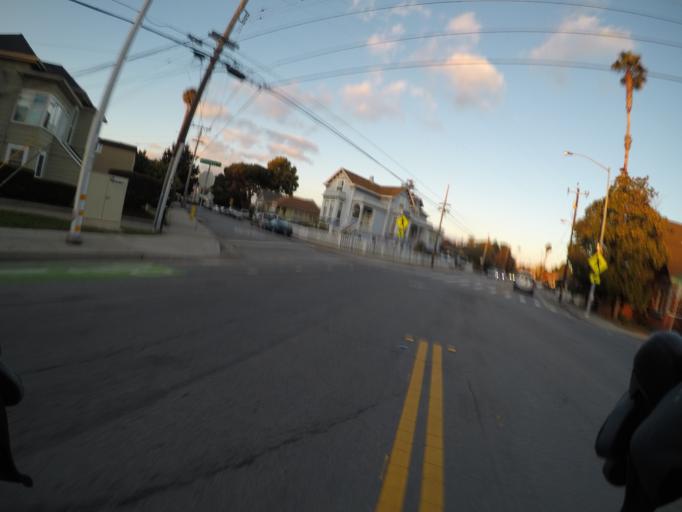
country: US
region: California
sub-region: Santa Cruz County
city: Santa Cruz
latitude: 36.9717
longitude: -122.0217
